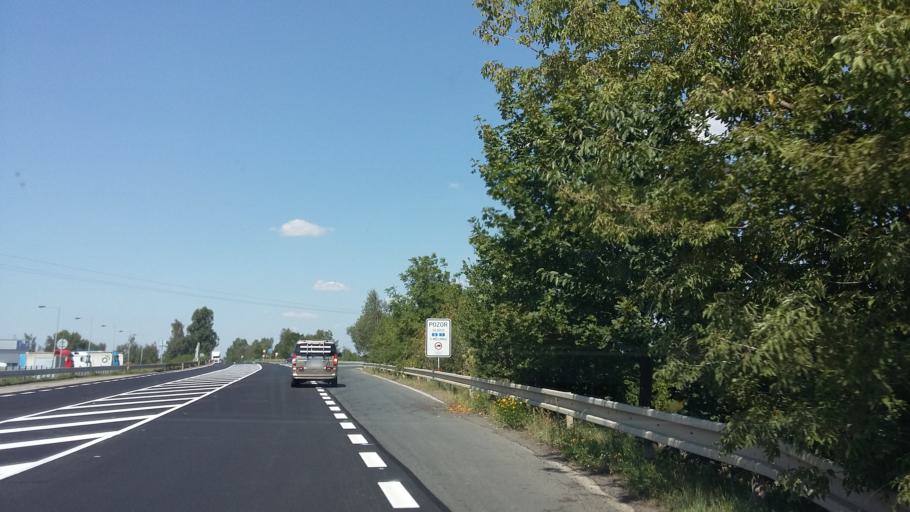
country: CZ
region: Central Bohemia
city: Brandys nad Labem-Stara Boleslav
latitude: 50.1673
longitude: 14.6749
